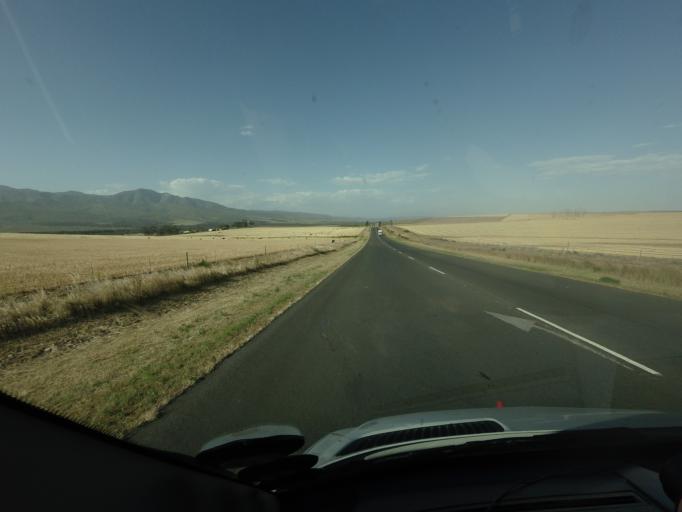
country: ZA
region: Western Cape
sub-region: Cape Winelands District Municipality
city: Ashton
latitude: -34.1543
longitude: 19.9695
